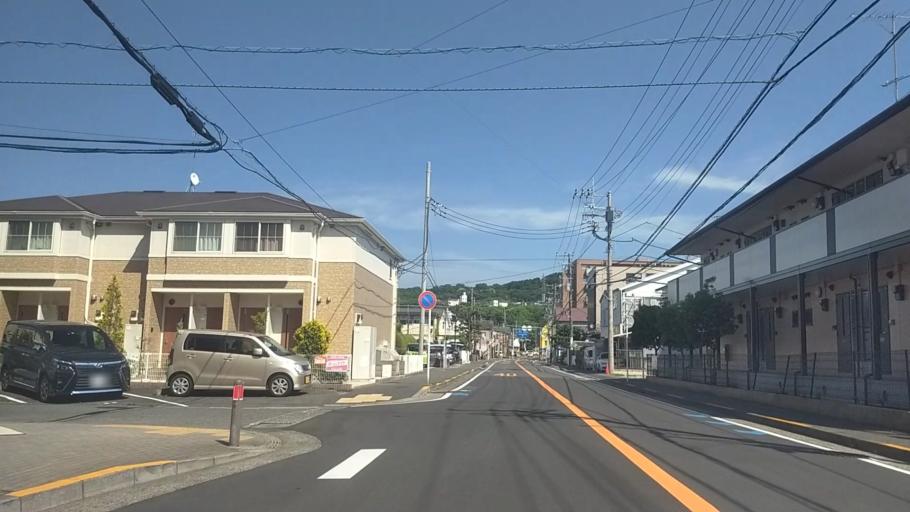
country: JP
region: Kanagawa
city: Kamakura
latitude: 35.3475
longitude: 139.5391
